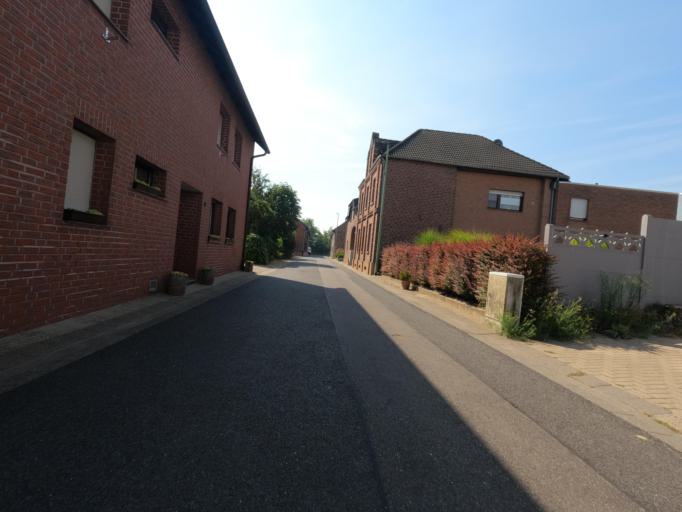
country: DE
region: North Rhine-Westphalia
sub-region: Regierungsbezirk Koln
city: Titz
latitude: 51.0048
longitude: 6.3663
